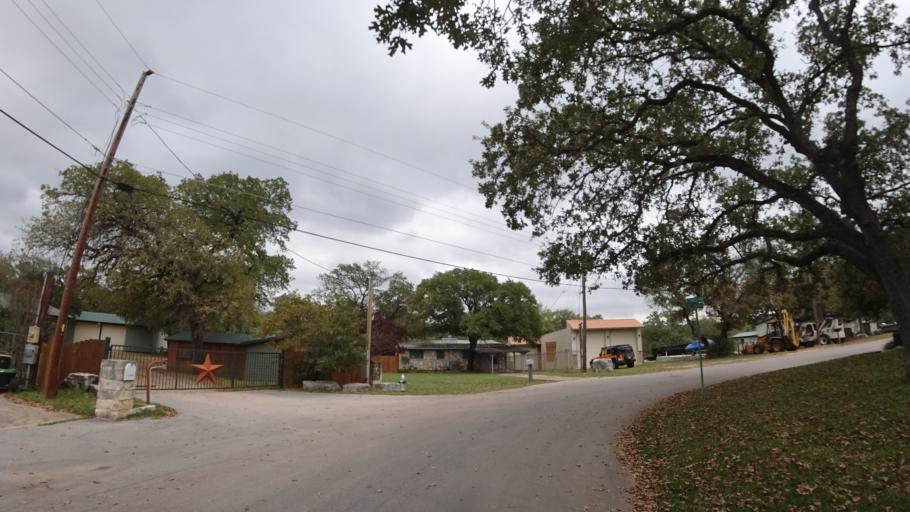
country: US
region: Texas
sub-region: Travis County
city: Bee Cave
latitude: 30.3336
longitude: -97.9266
